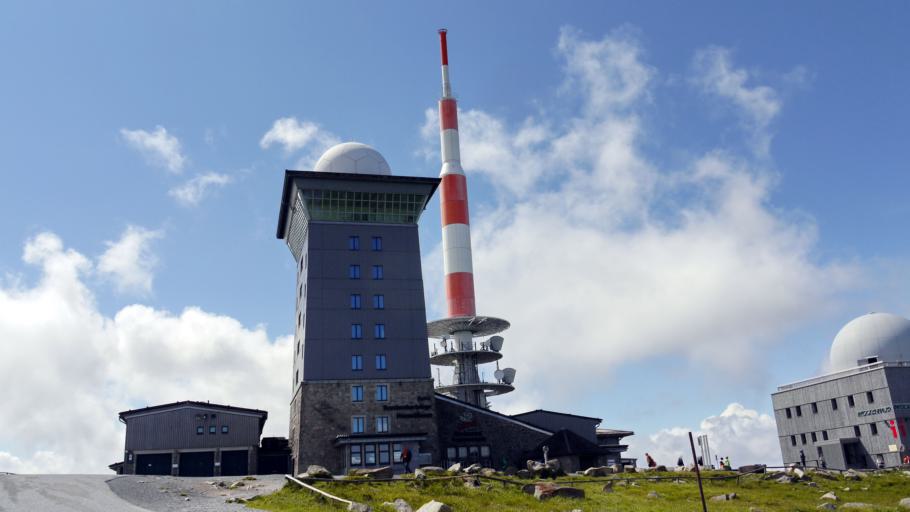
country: DE
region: Lower Saxony
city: Braunlage
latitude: 51.7996
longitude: 10.6167
